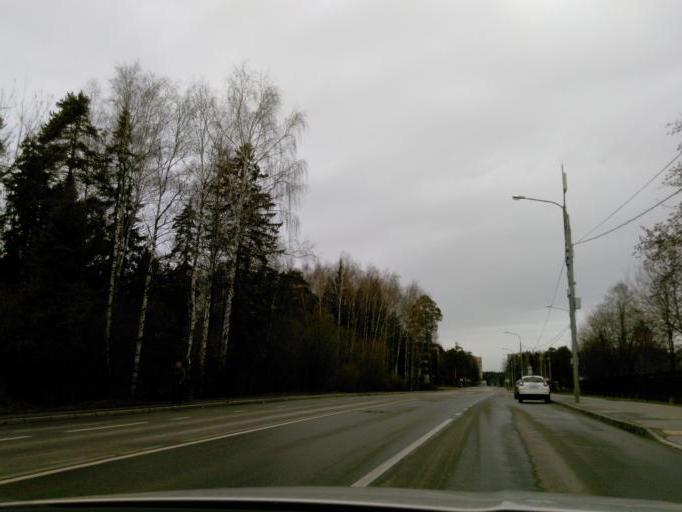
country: RU
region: Moskovskaya
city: Rzhavki
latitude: 55.9933
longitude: 37.2454
